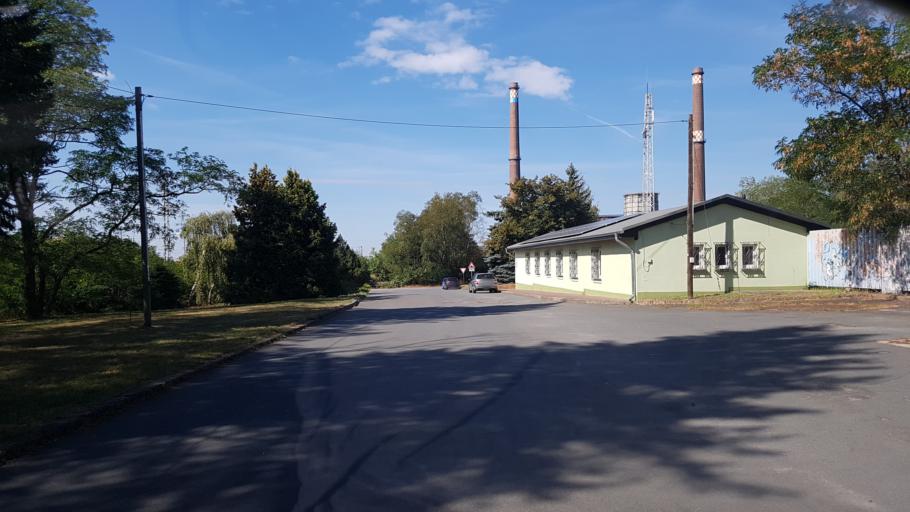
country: DE
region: Brandenburg
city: Plessa
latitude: 51.4718
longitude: 13.6194
